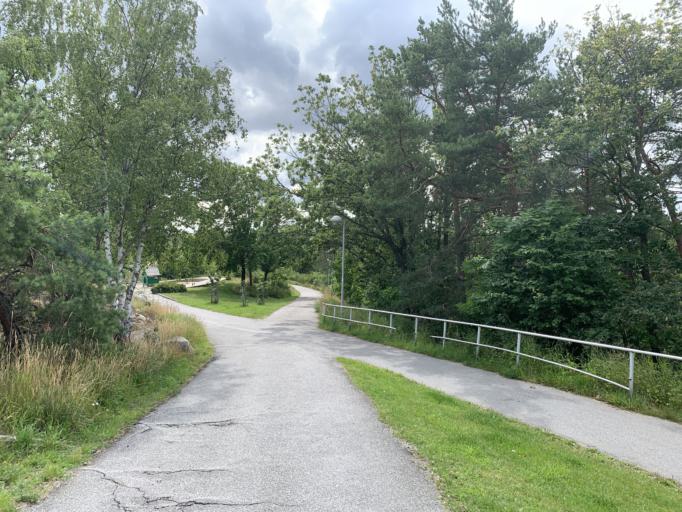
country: SE
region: Stockholm
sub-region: Sundbybergs Kommun
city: Sundbyberg
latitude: 59.3750
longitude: 17.9621
